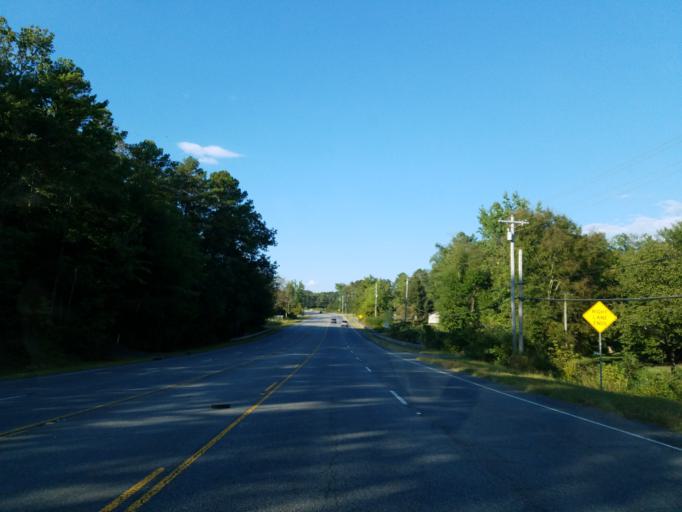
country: US
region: Georgia
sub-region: Murray County
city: Chatsworth
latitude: 34.8522
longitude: -84.7542
